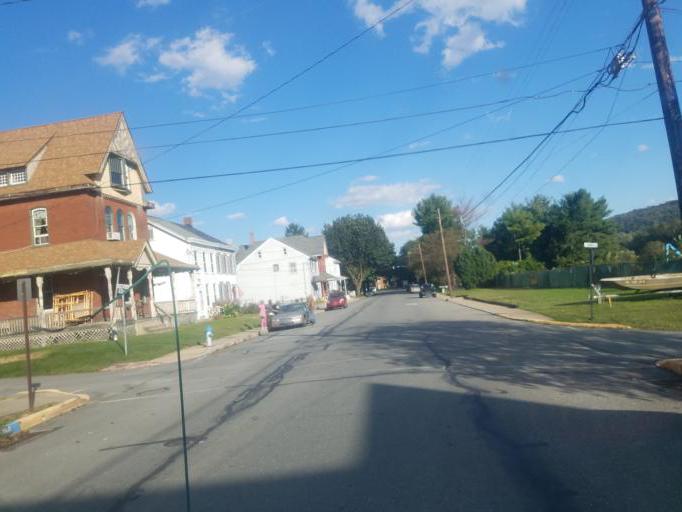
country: US
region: Pennsylvania
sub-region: Lancaster County
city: Marietta
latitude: 40.0555
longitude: -76.5647
